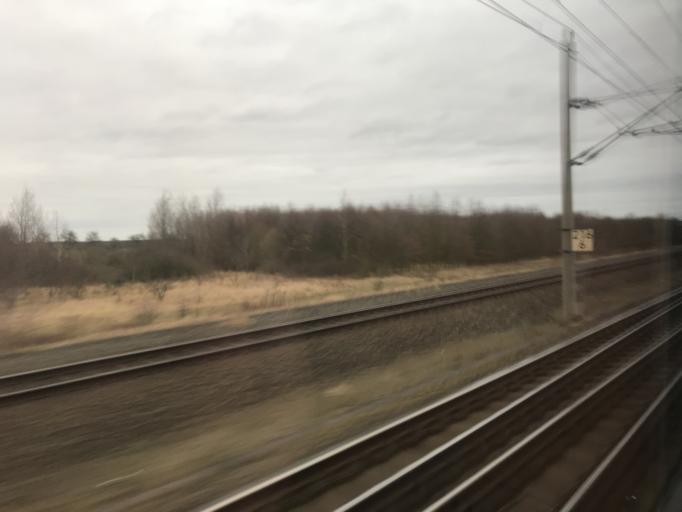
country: DE
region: Saxony-Anhalt
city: Luderitz
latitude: 52.5736
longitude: 11.6975
